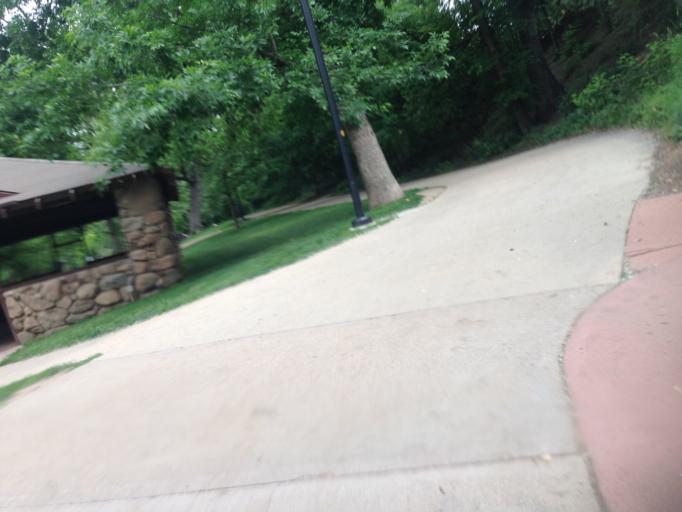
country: US
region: Colorado
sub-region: Boulder County
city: Boulder
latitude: 40.0129
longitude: -105.2961
